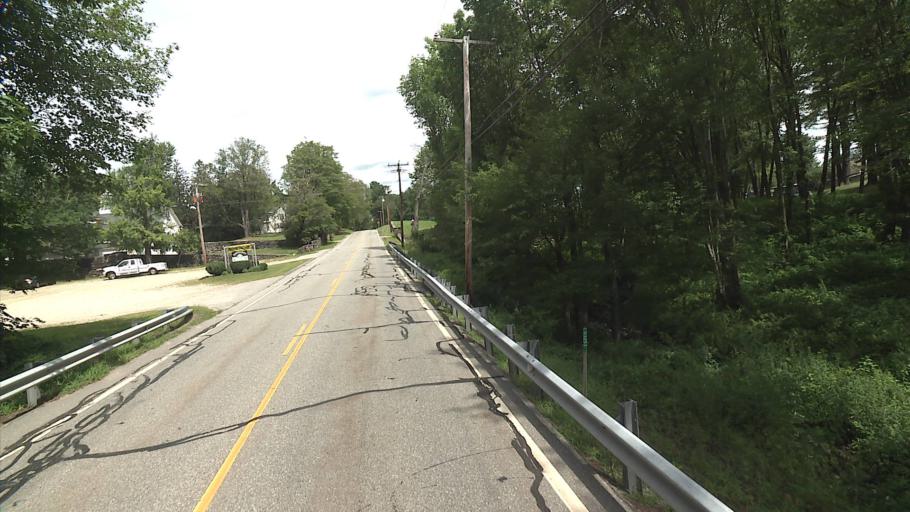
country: US
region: Connecticut
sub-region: Windham County
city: Thompson
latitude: 41.9369
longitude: -71.8663
